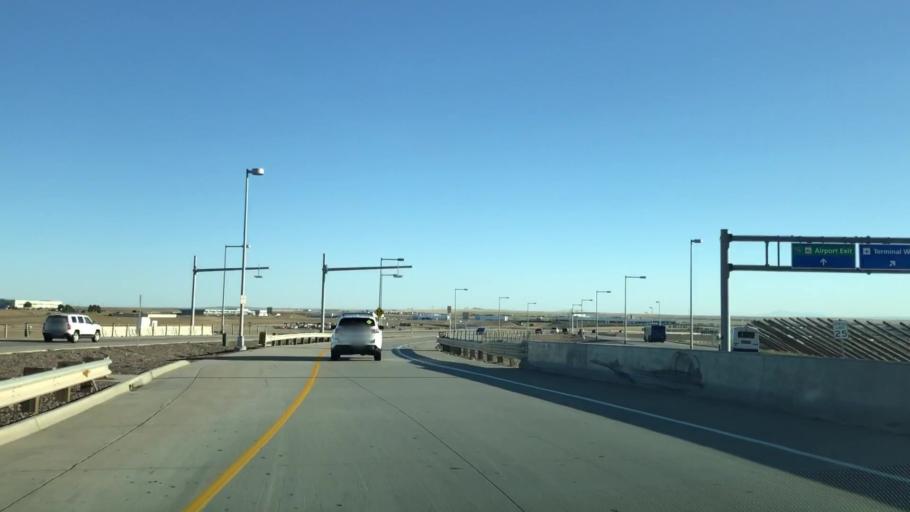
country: US
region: Colorado
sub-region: Weld County
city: Lochbuie
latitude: 39.8464
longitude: -104.6726
